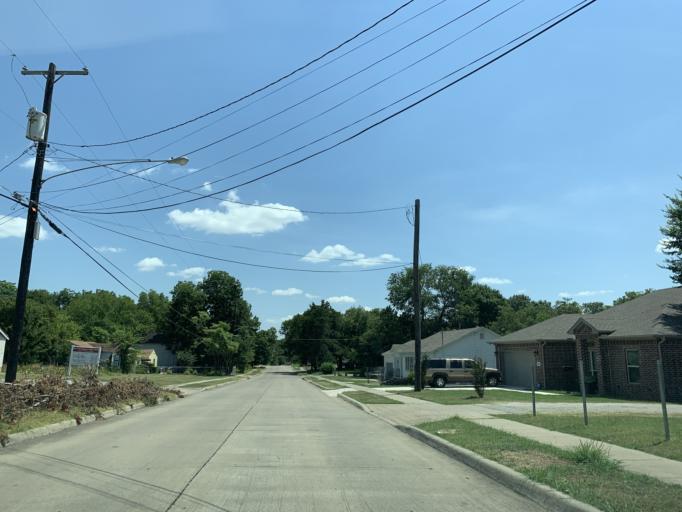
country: US
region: Texas
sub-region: Dallas County
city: Hutchins
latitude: 32.6882
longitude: -96.7786
